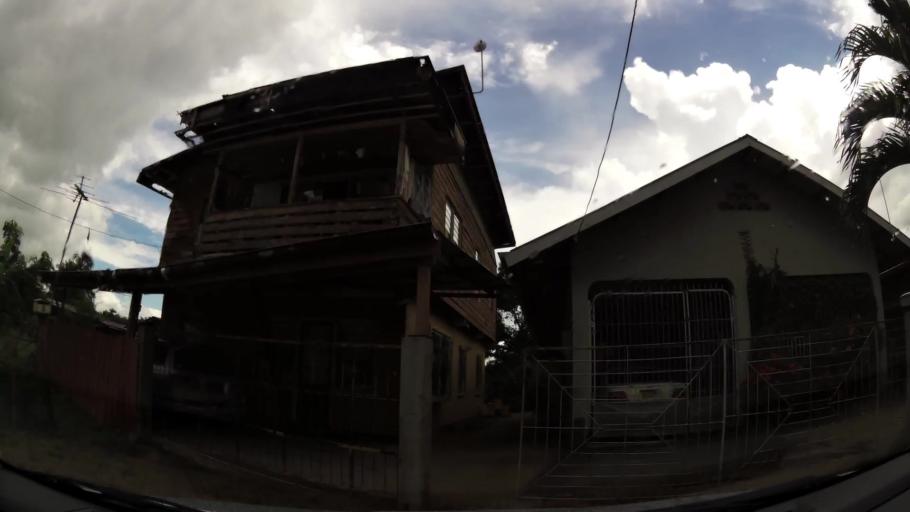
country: SR
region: Paramaribo
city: Paramaribo
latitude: 5.7901
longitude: -55.1993
